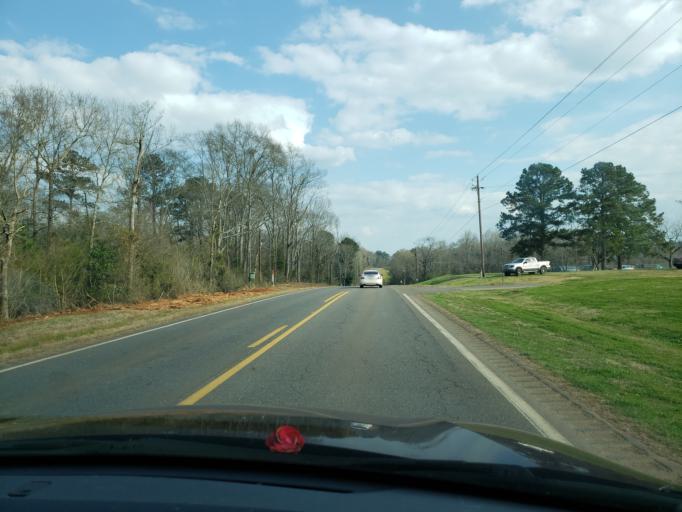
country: US
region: Alabama
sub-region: Hale County
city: Greensboro
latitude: 32.7132
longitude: -87.6149
